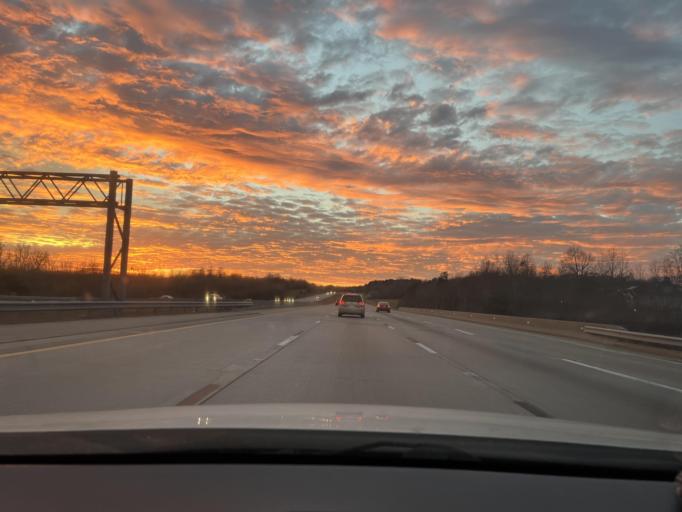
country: US
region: North Carolina
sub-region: Guilford County
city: Forest Oaks
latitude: 36.0323
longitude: -79.7013
